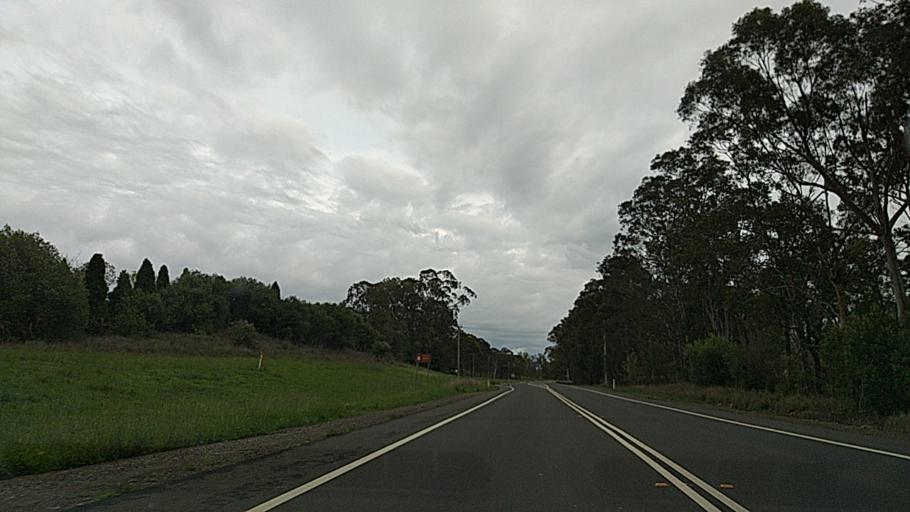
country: AU
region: New South Wales
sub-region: Camden
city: Camden South
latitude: -34.1166
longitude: 150.6979
